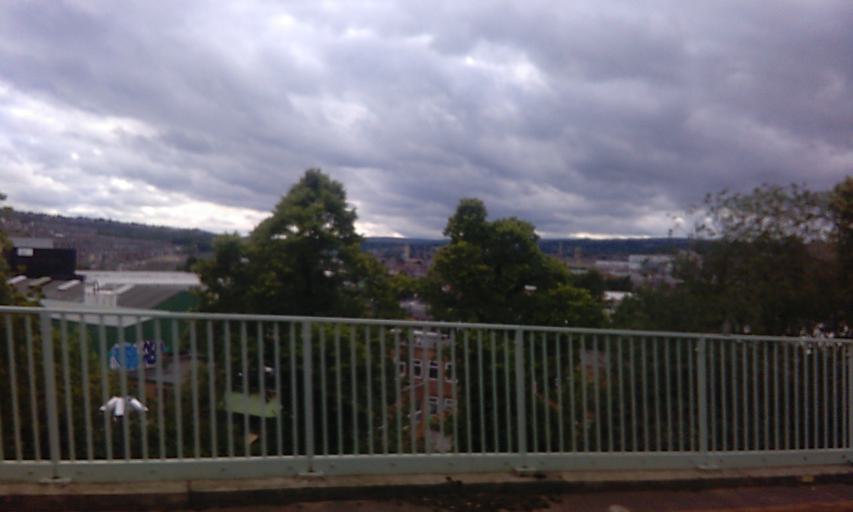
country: GB
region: England
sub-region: Sheffield
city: Sheffield
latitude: 53.3712
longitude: -1.4603
